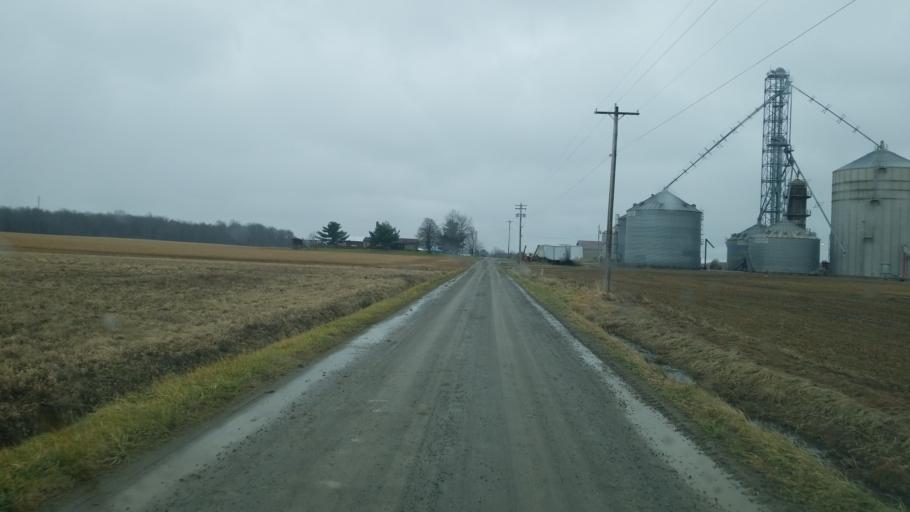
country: US
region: Ohio
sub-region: Ashtabula County
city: Roaming Shores
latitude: 41.5835
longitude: -80.7193
